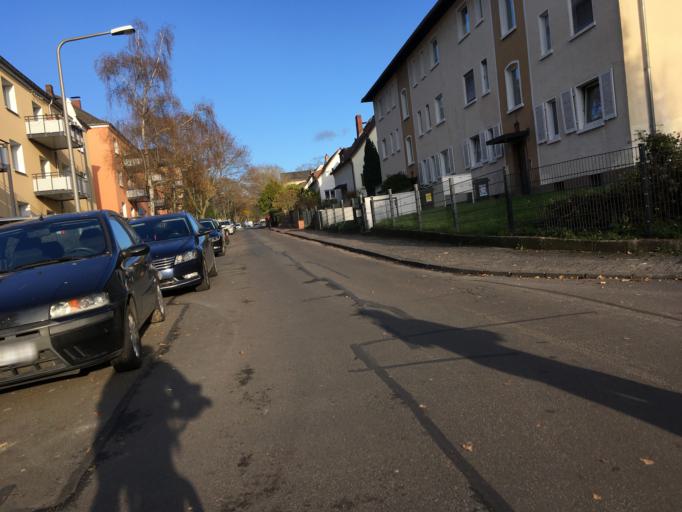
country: DE
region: Hesse
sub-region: Regierungsbezirk Darmstadt
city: Wiesbaden
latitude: 50.0617
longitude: 8.2296
